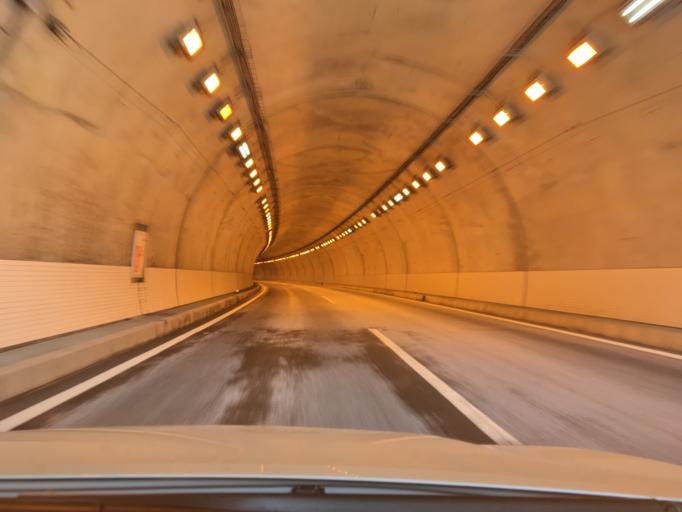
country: JP
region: Yamagata
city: Yamagata-shi
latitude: 38.2821
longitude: 140.3741
